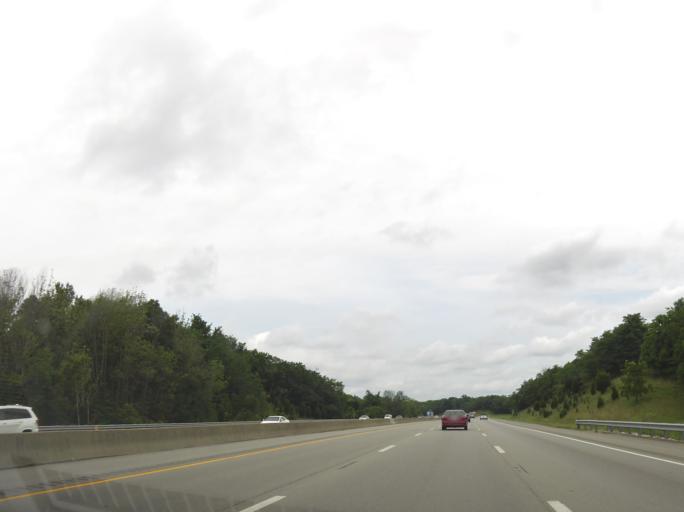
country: US
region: Kentucky
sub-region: Scott County
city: Georgetown
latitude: 38.3152
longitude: -84.5585
